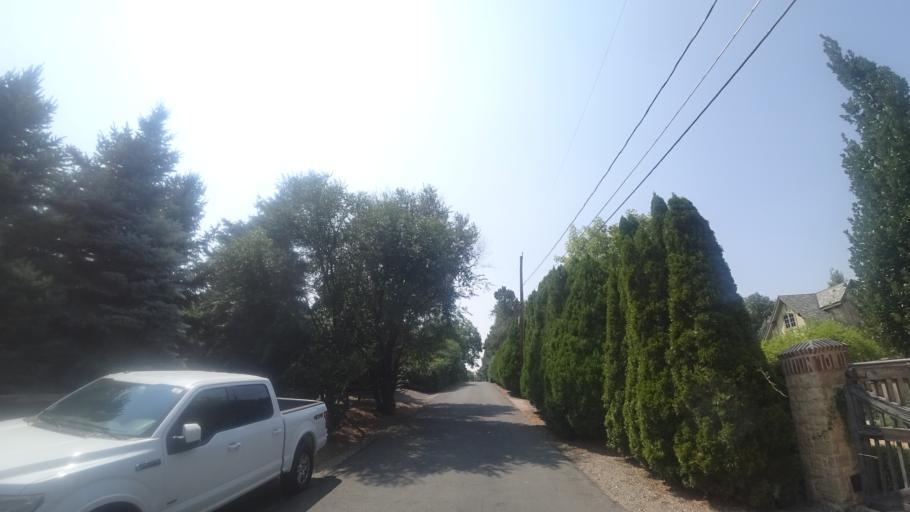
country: US
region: Colorado
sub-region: Arapahoe County
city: Cherry Hills Village
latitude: 39.6333
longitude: -104.9682
